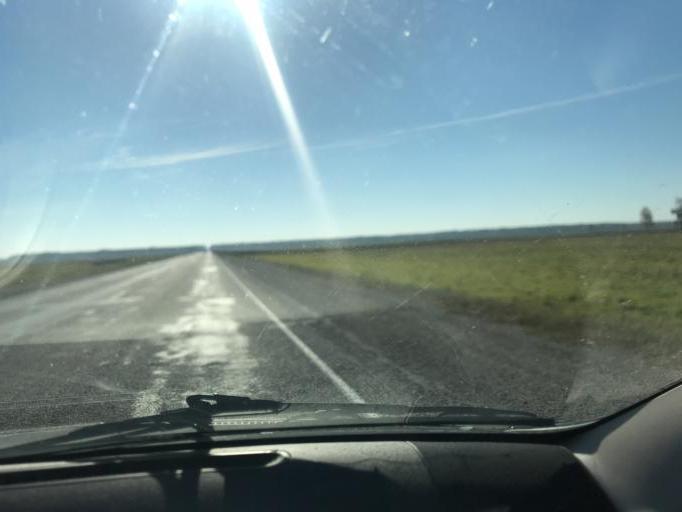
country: BY
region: Minsk
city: Starobin
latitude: 52.5267
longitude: 27.4740
